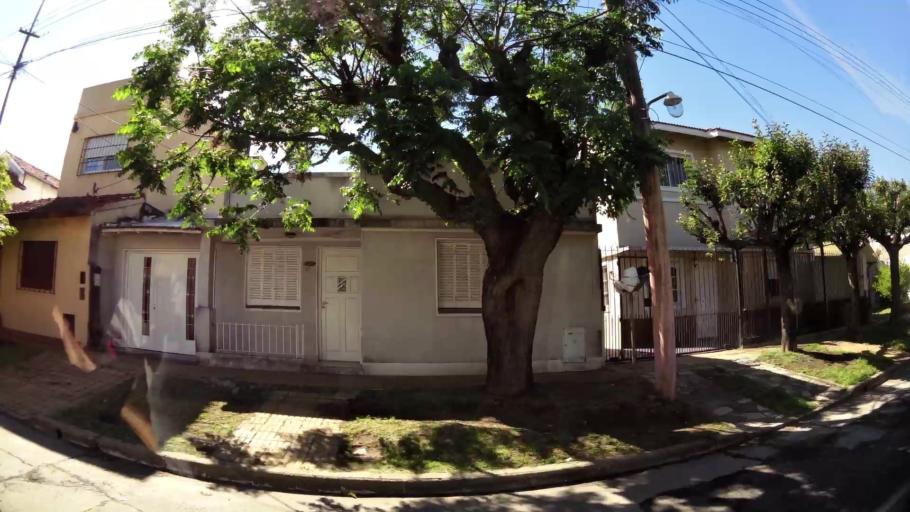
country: AR
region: Buenos Aires
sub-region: Partido de Quilmes
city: Quilmes
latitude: -34.7029
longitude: -58.2904
